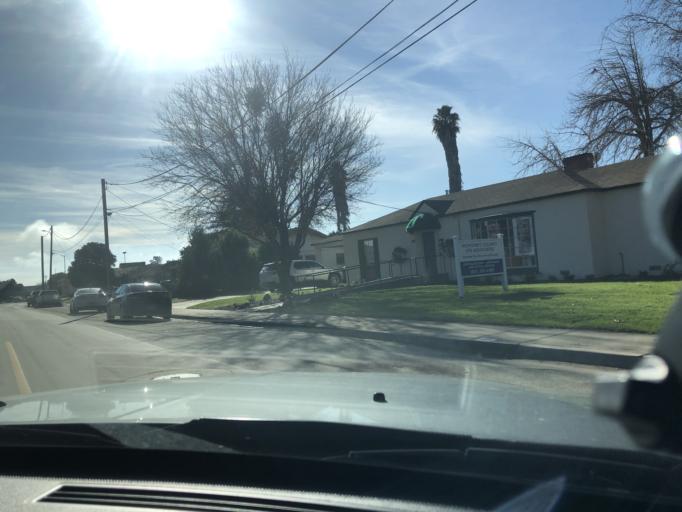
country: US
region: California
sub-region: Monterey County
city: King City
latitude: 36.2060
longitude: -121.1315
